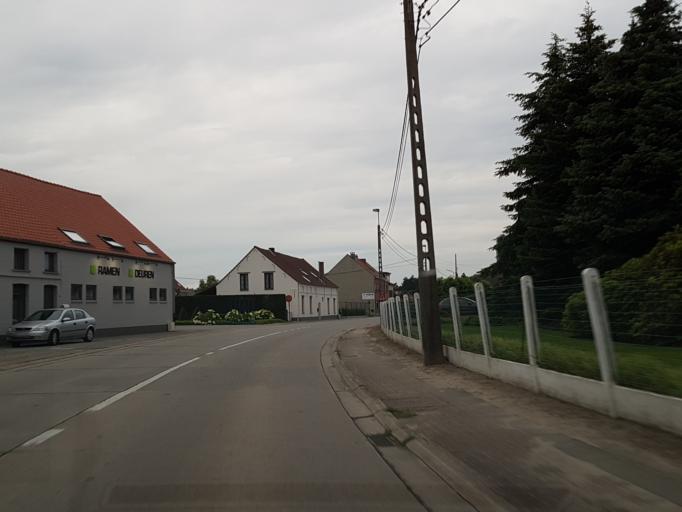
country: BE
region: Flanders
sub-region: Provincie Vlaams-Brabant
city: Kapelle-op-den-Bos
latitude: 51.0024
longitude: 4.3610
